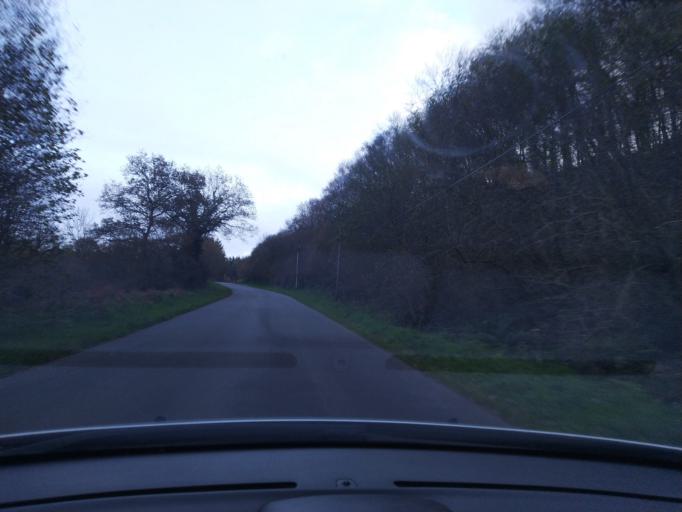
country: FR
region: Brittany
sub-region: Departement du Finistere
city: Guerlesquin
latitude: 48.5336
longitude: -3.6116
